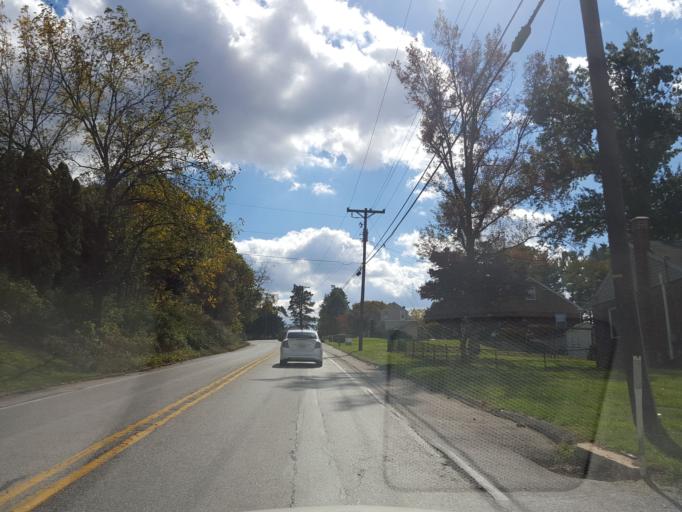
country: US
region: Pennsylvania
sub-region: York County
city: Yoe
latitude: 39.9366
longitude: -76.6442
